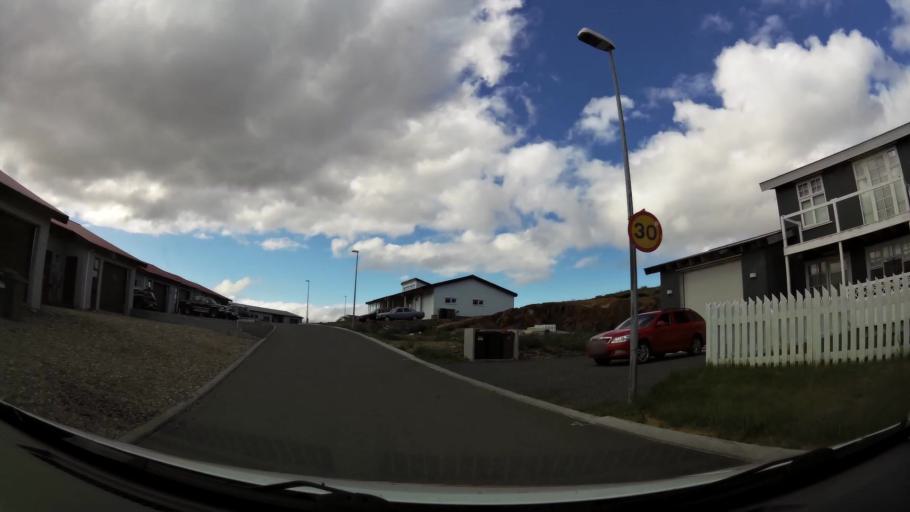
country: IS
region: East
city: Egilsstadir
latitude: 65.2585
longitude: -14.3808
